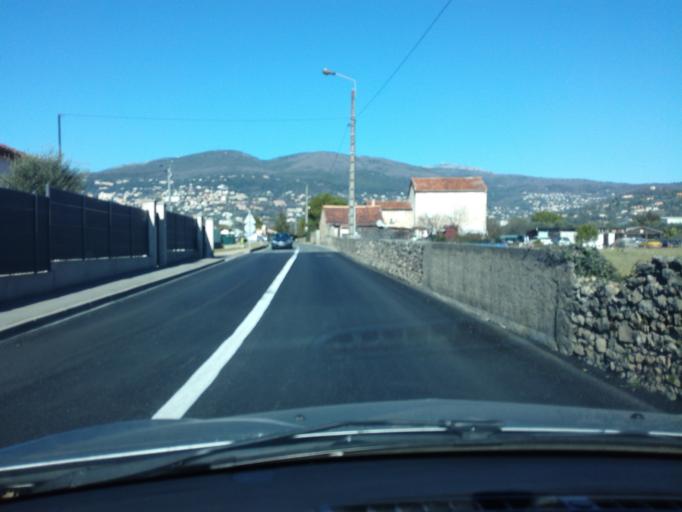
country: FR
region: Provence-Alpes-Cote d'Azur
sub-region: Departement des Alpes-Maritimes
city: Mouans-Sartoux
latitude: 43.6446
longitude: 6.9542
